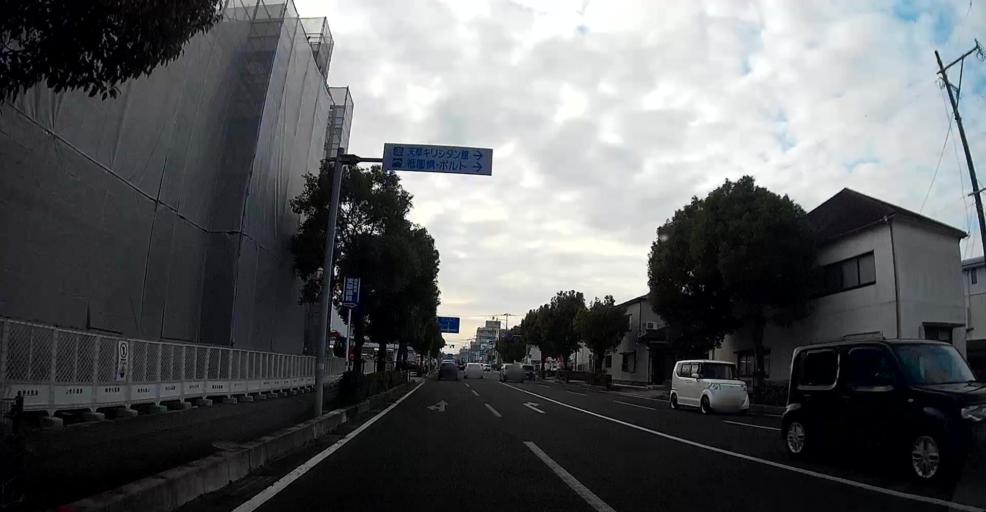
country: JP
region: Kumamoto
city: Hondo
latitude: 32.4608
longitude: 130.1917
